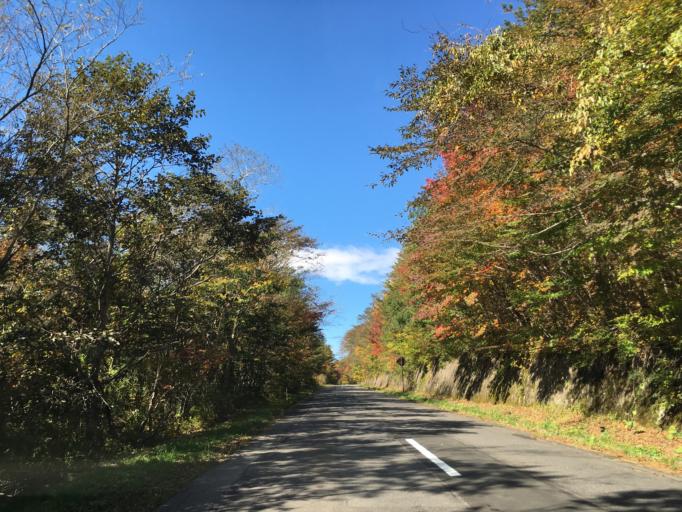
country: JP
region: Fukushima
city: Inawashiro
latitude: 37.5803
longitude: 140.2466
